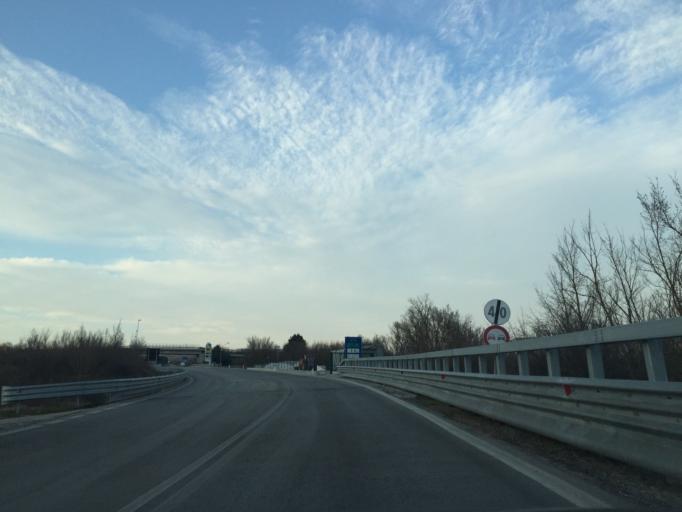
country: IT
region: Molise
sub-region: Provincia di Campobasso
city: Guardiaregia
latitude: 41.4652
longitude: 14.5591
